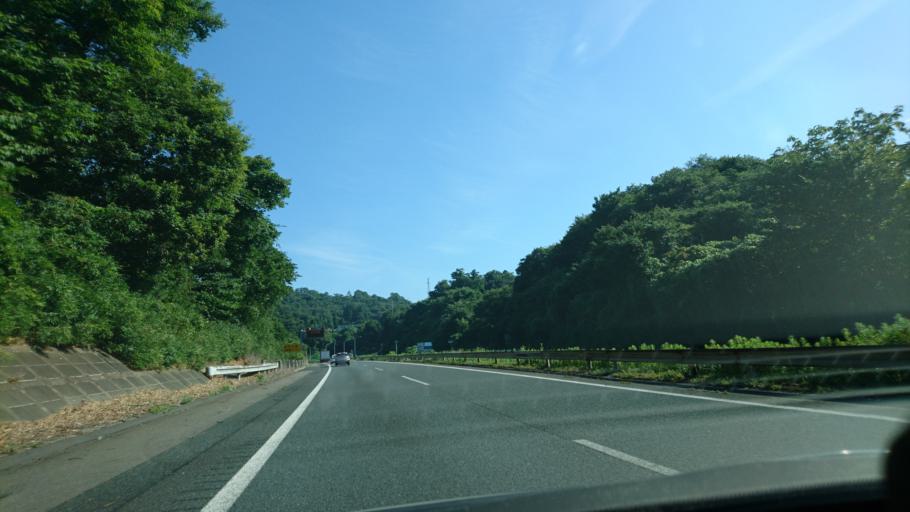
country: JP
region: Iwate
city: Ichinoseki
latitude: 38.9442
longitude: 141.1038
